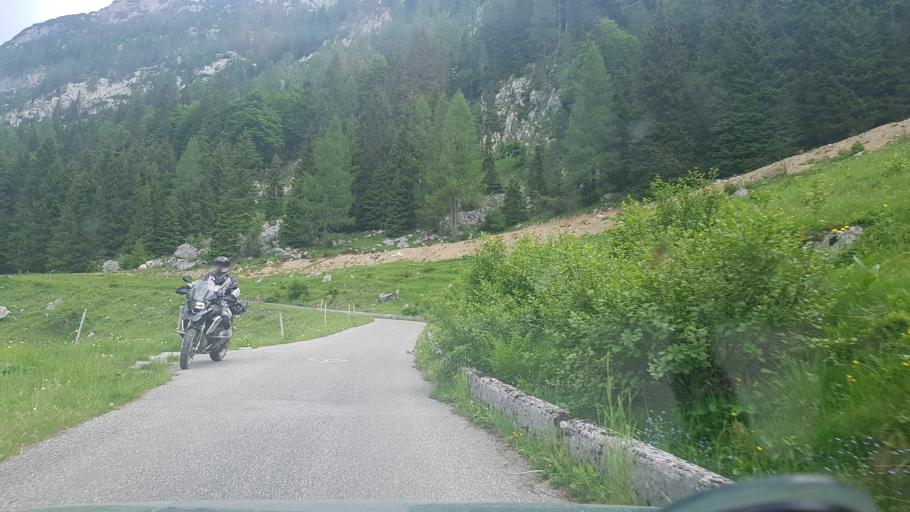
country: IT
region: Friuli Venezia Giulia
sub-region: Provincia di Udine
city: Paularo
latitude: 46.5542
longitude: 13.1917
